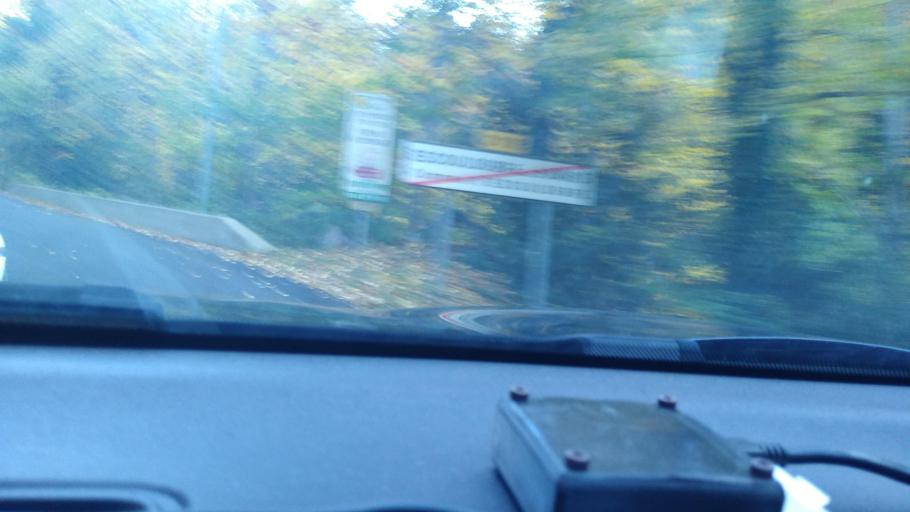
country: FR
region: Languedoc-Roussillon
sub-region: Departement de l'Aude
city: Quillan
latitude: 42.7183
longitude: 2.1259
